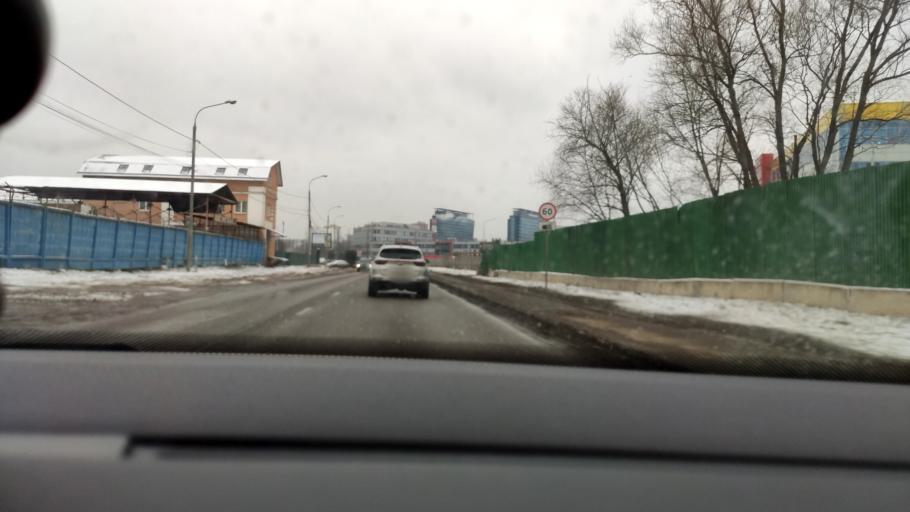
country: RU
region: Moscow
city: Khimki
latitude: 55.9149
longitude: 37.4208
